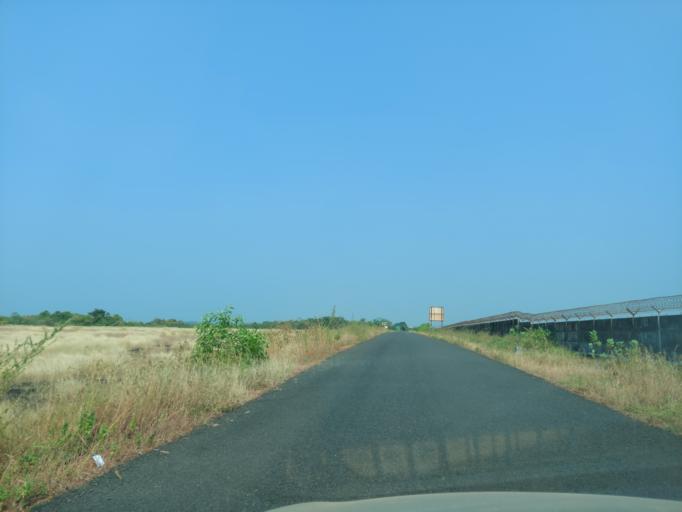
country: IN
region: Maharashtra
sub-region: Sindhudurg
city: Malvan
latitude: 15.9988
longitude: 73.5087
